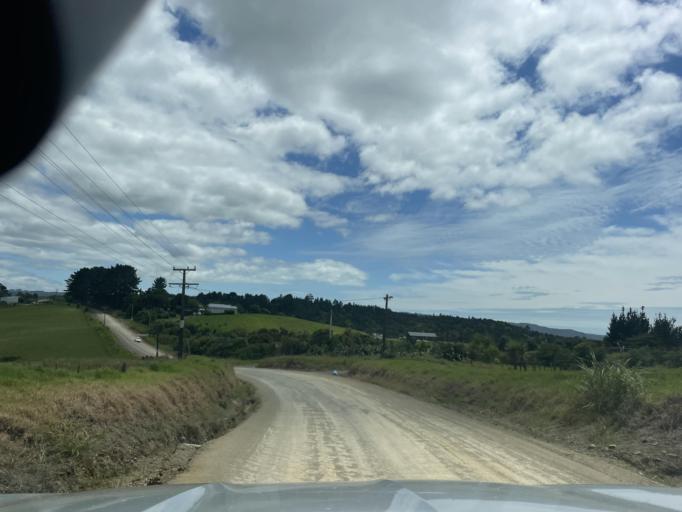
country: NZ
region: Auckland
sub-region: Auckland
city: Wellsford
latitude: -36.1424
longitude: 174.5403
